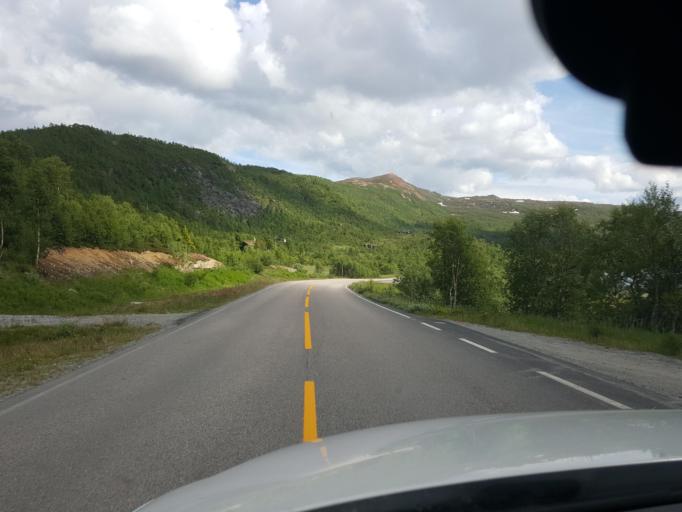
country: NO
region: Nordland
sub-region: Rana
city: Mo i Rana
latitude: 66.2876
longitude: 14.5085
